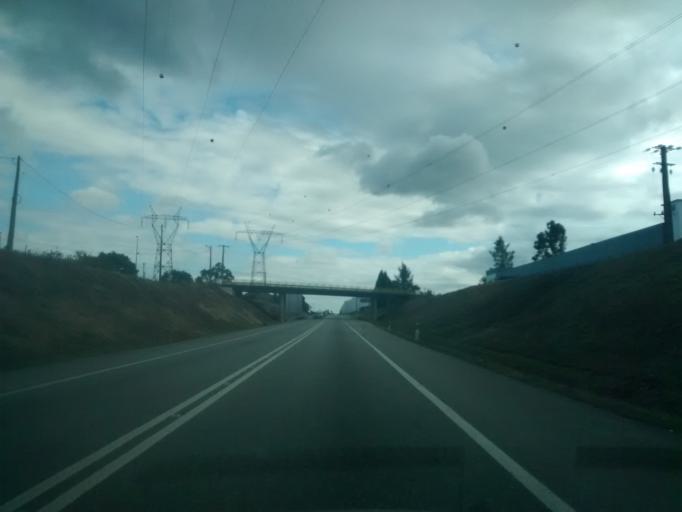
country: PT
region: Aveiro
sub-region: Agueda
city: Agueda
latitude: 40.5820
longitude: -8.4730
